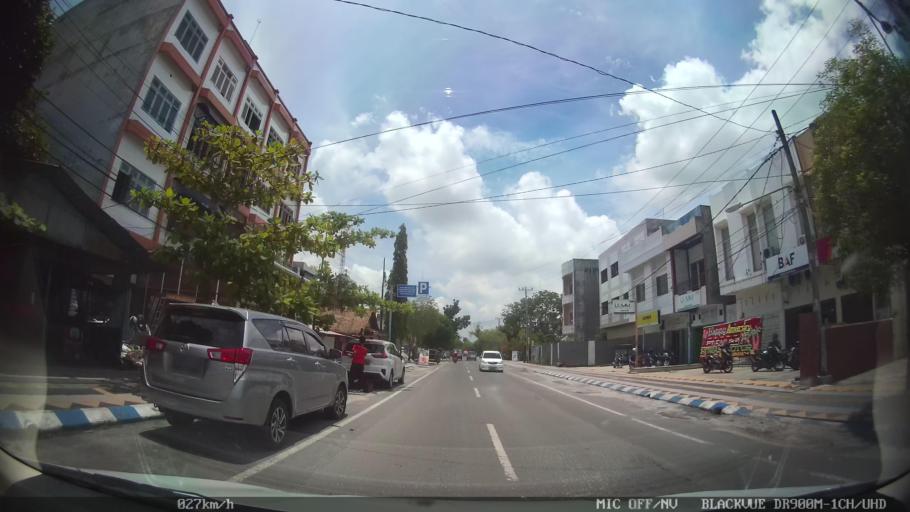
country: ID
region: North Sumatra
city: Percut
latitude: 3.5601
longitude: 98.8737
